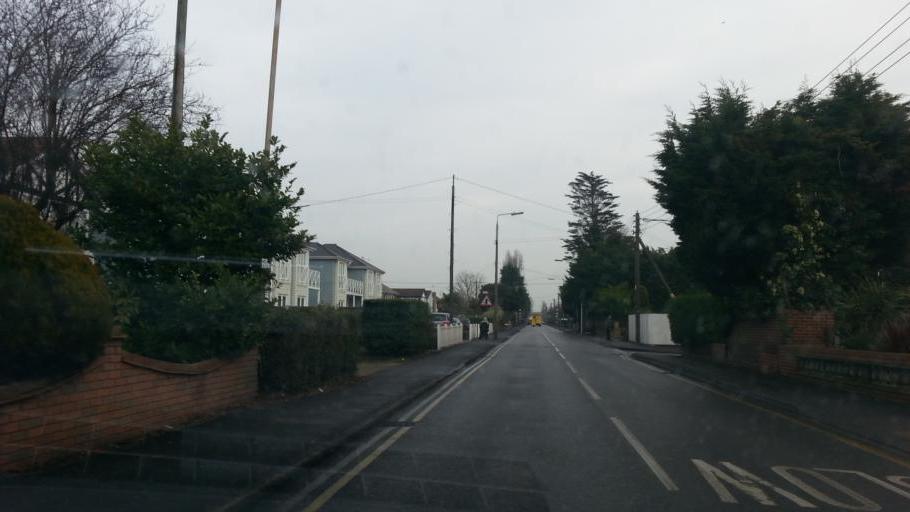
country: GB
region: England
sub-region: Essex
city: Canvey Island
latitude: 51.5202
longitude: 0.5833
